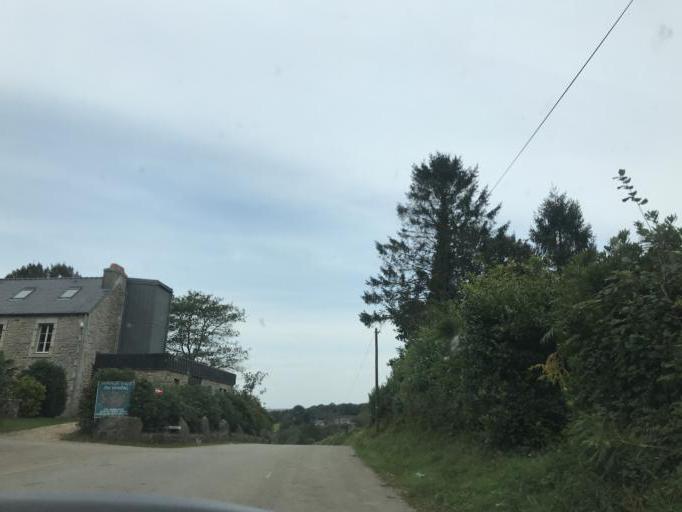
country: FR
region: Brittany
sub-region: Departement du Finistere
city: Plouneour-Menez
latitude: 48.3685
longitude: -3.8625
